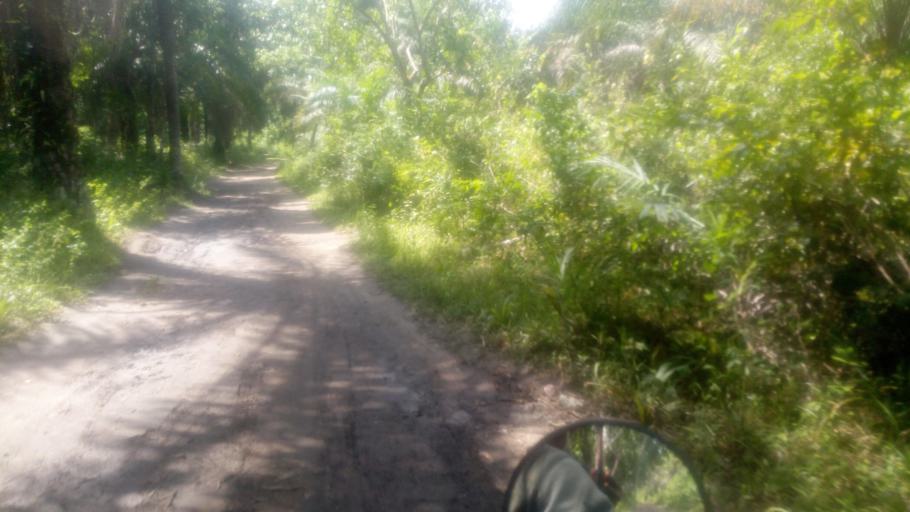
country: SL
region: Northern Province
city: Magburaka
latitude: 8.6610
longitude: -12.0695
